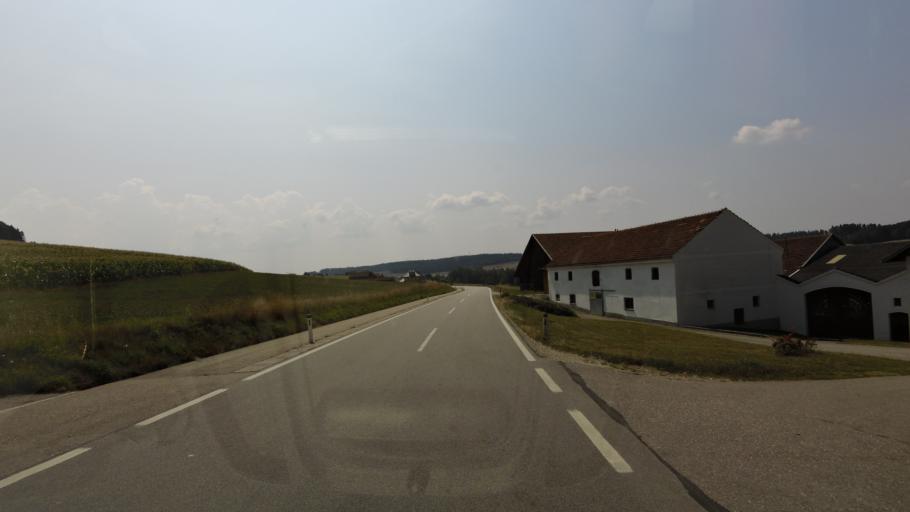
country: DE
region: Bavaria
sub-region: Lower Bavaria
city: Bad Fussing
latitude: 48.2527
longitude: 13.3380
